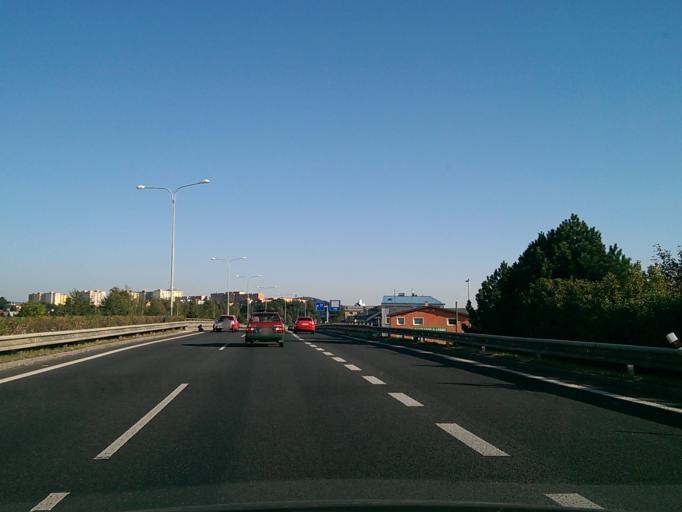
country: CZ
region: Liberecky
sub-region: Okres Liberec
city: Liberec
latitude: 50.7588
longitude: 15.0497
